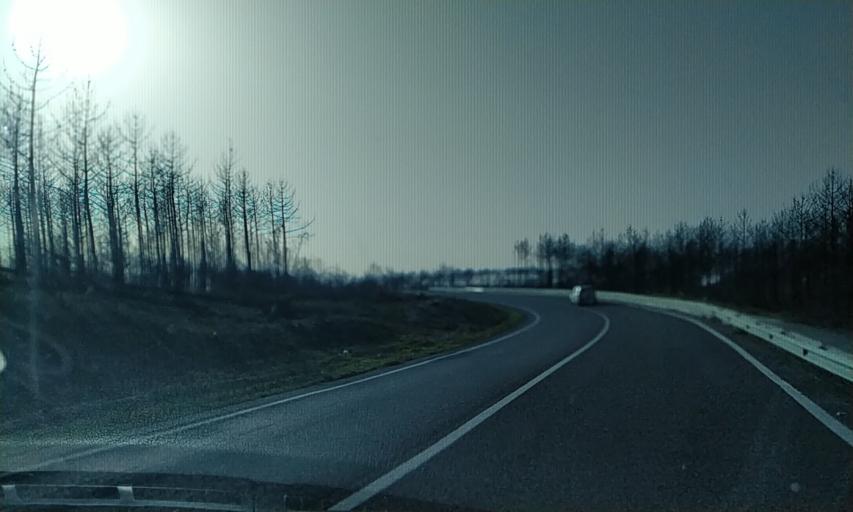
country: PT
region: Leiria
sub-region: Marinha Grande
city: Marinha Grande
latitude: 39.7492
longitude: -9.0060
